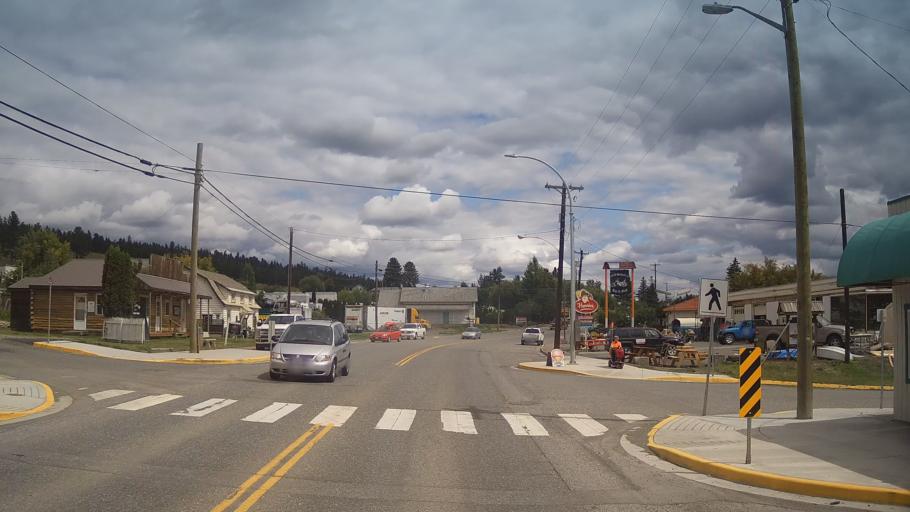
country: CA
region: British Columbia
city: Cache Creek
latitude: 51.0934
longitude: -121.5841
